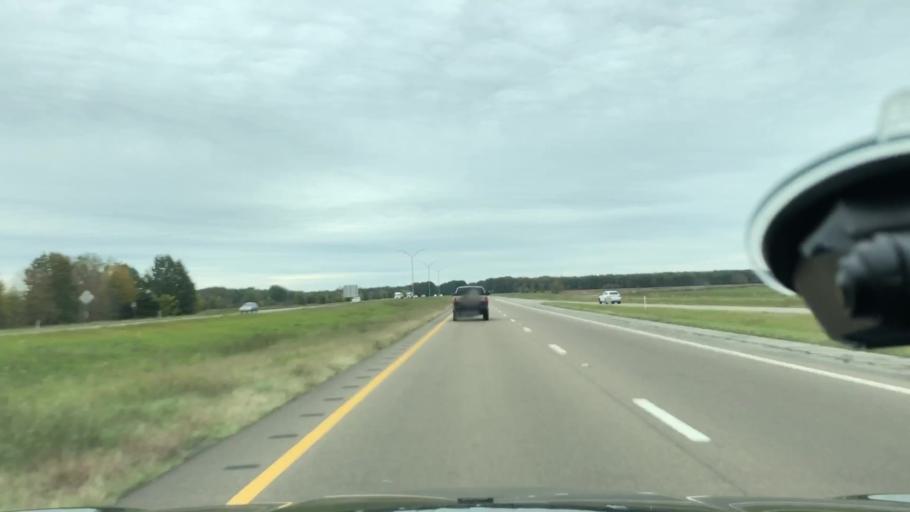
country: US
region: Texas
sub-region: Morris County
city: Naples
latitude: 33.2946
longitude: -94.7346
